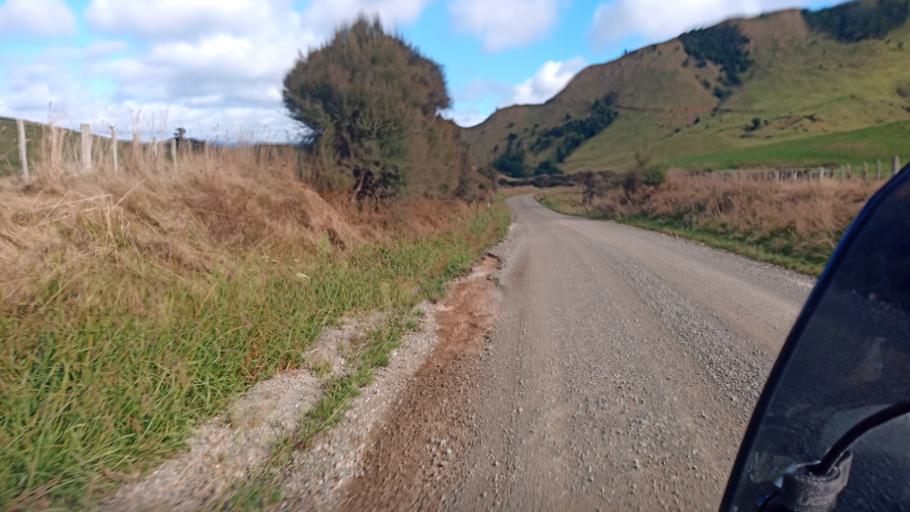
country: NZ
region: Bay of Plenty
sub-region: Opotiki District
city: Opotiki
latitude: -38.4541
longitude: 177.4000
